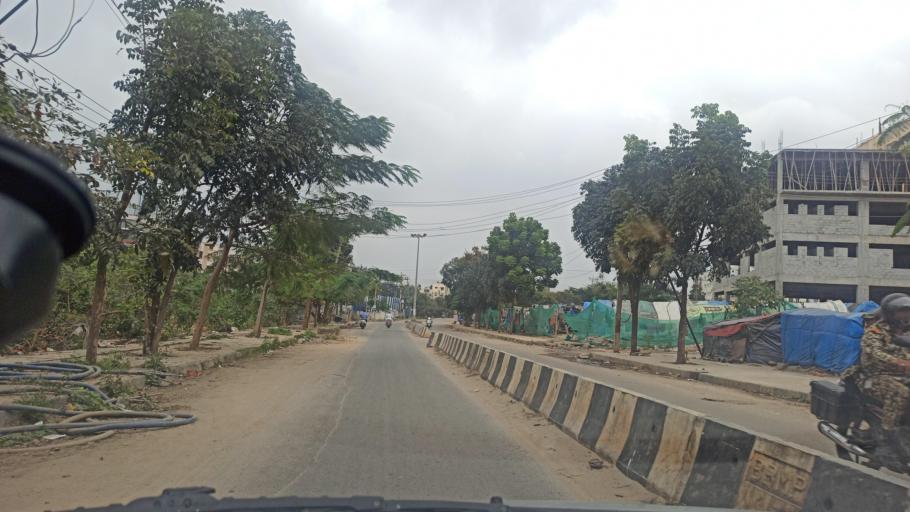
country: IN
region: Karnataka
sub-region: Bangalore Urban
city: Yelahanka
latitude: 13.0385
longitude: 77.6166
